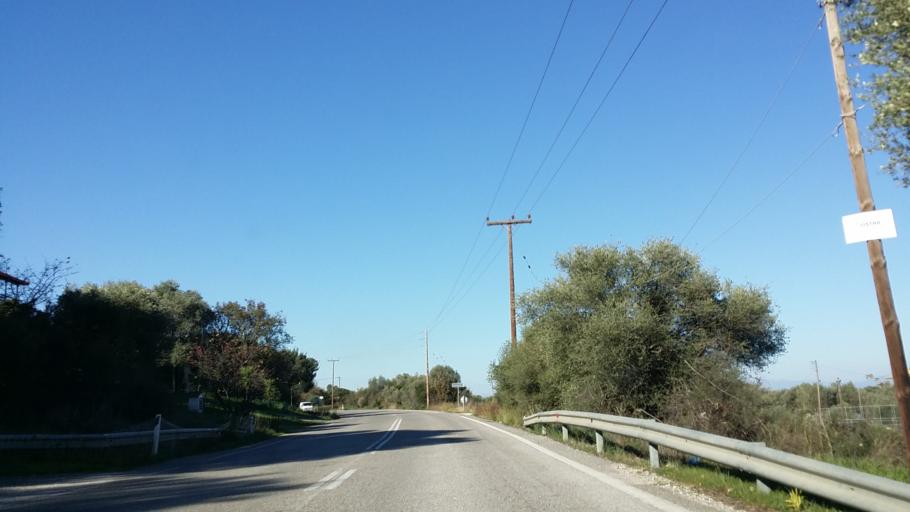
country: GR
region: West Greece
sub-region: Nomos Aitolias kai Akarnanias
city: Amfilochia
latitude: 38.8652
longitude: 21.0754
